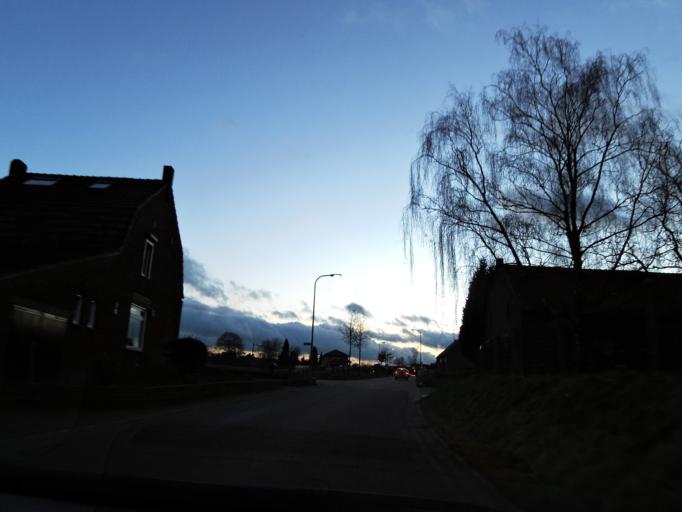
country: NL
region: Limburg
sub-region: Gemeente Roermond
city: Leeuwen
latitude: 51.2138
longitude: 6.0032
